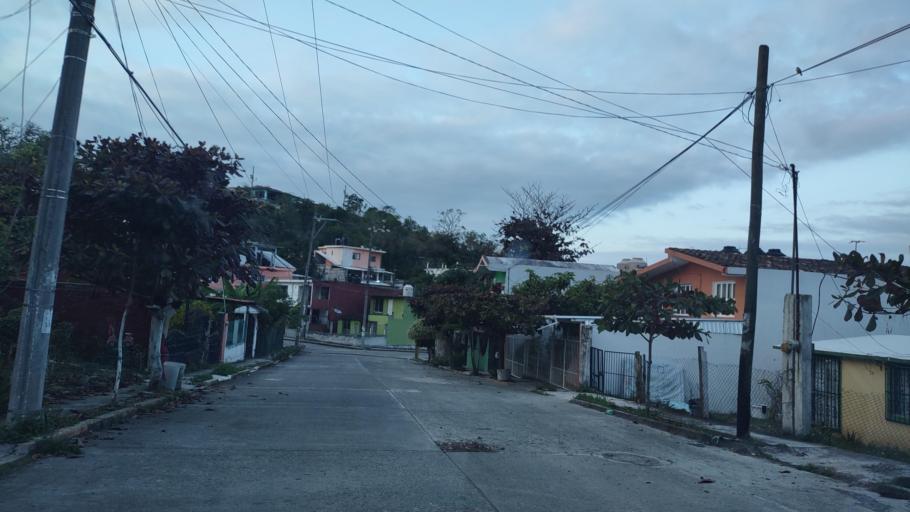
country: MX
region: Veracruz
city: Papantla de Olarte
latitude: 20.4600
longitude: -97.3071
